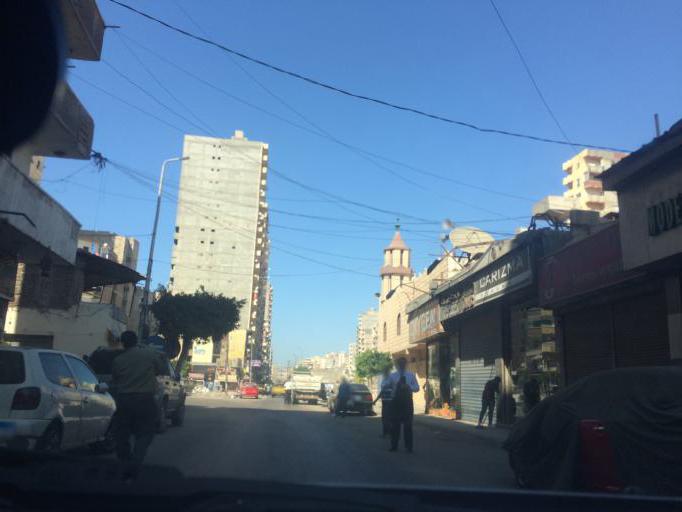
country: EG
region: Alexandria
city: Alexandria
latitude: 31.2525
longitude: 29.9862
